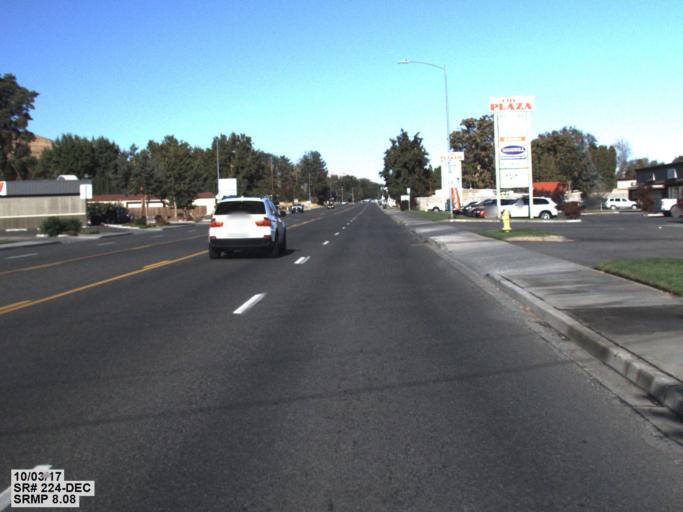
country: US
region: Washington
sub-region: Benton County
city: West Richland
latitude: 46.2975
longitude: -119.3398
